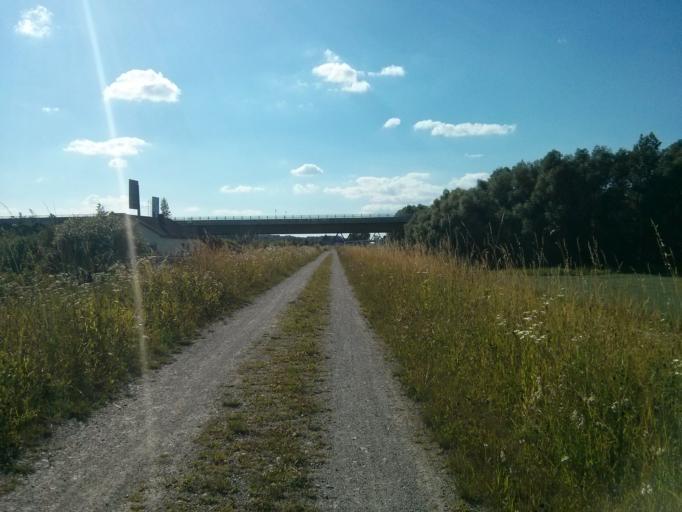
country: DE
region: Bavaria
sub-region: Lower Bavaria
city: Deggendorf
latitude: 48.8256
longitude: 12.9485
